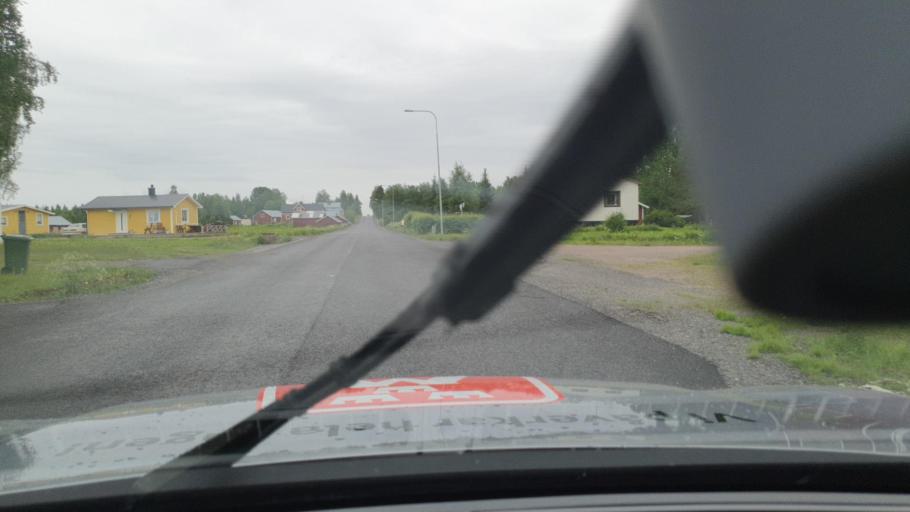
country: SE
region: Norrbotten
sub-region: Pajala Kommun
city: Pajala
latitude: 66.7311
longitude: 23.1769
